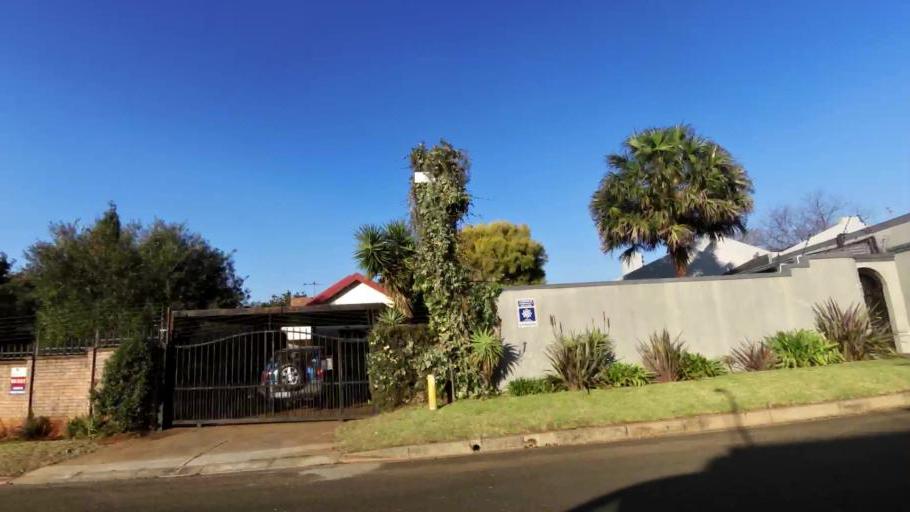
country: ZA
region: Gauteng
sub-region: City of Johannesburg Metropolitan Municipality
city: Johannesburg
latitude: -26.1597
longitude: 27.9854
